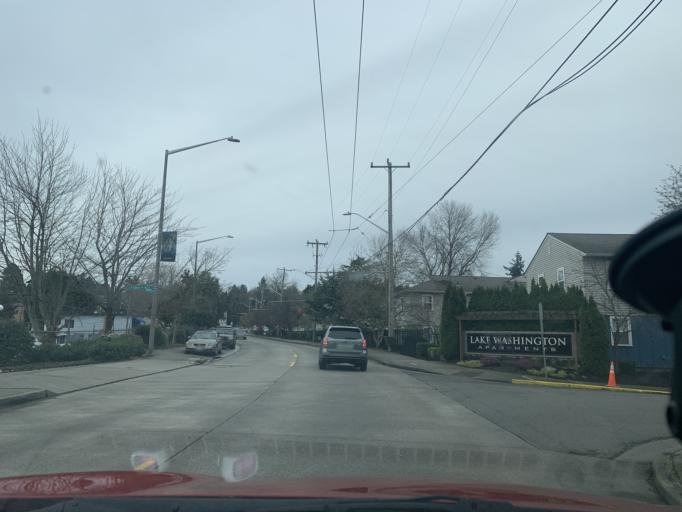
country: US
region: Washington
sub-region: King County
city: Bryn Mawr-Skyway
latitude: 47.5217
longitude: -122.2643
